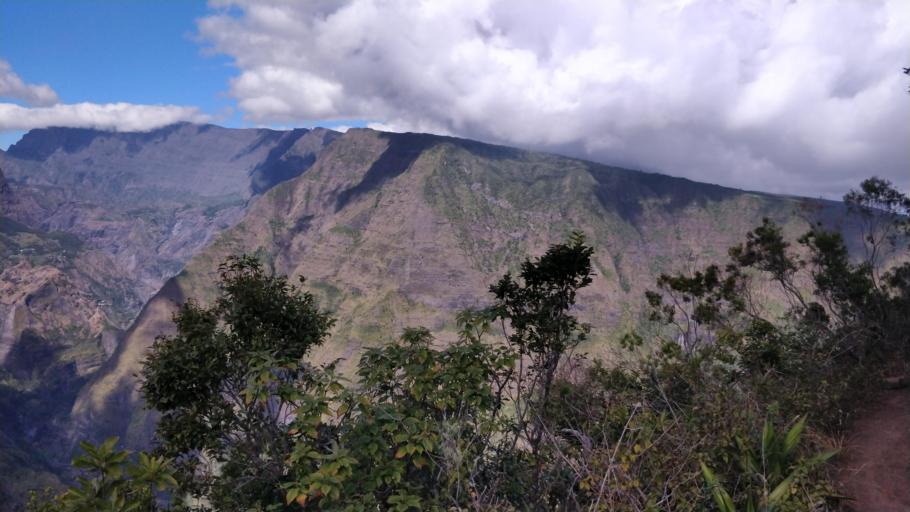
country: RE
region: Reunion
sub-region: Reunion
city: La Possession
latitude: -20.9876
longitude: 55.3947
